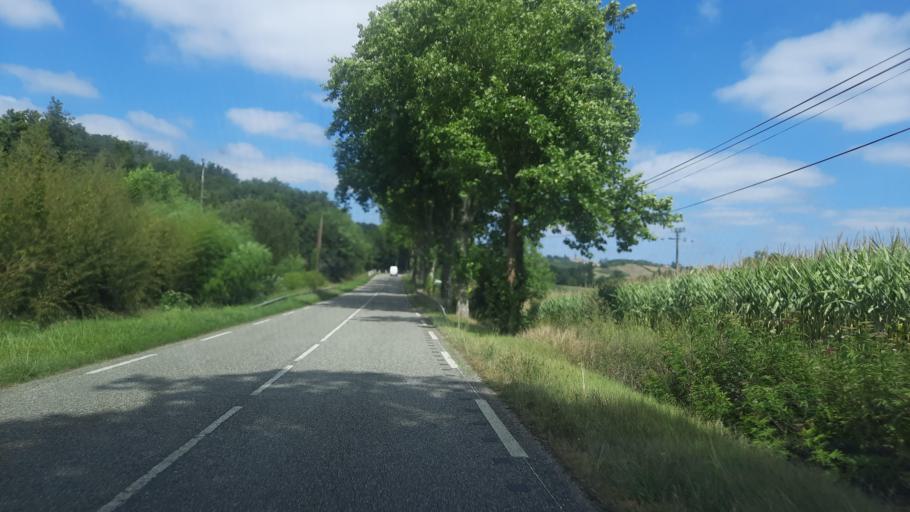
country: FR
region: Midi-Pyrenees
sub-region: Departement de la Haute-Garonne
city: Boulogne-sur-Gesse
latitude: 43.3641
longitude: 0.7402
